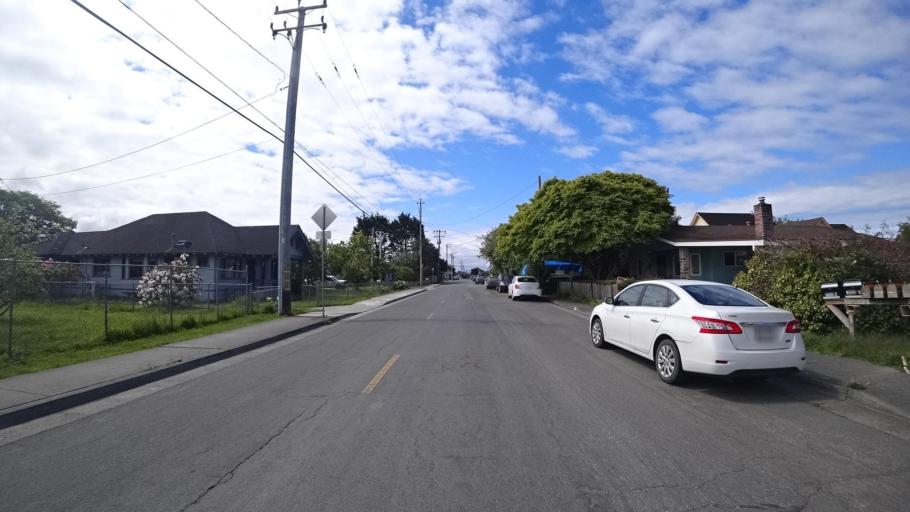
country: US
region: California
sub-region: Humboldt County
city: Arcata
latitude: 40.8747
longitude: -124.0949
